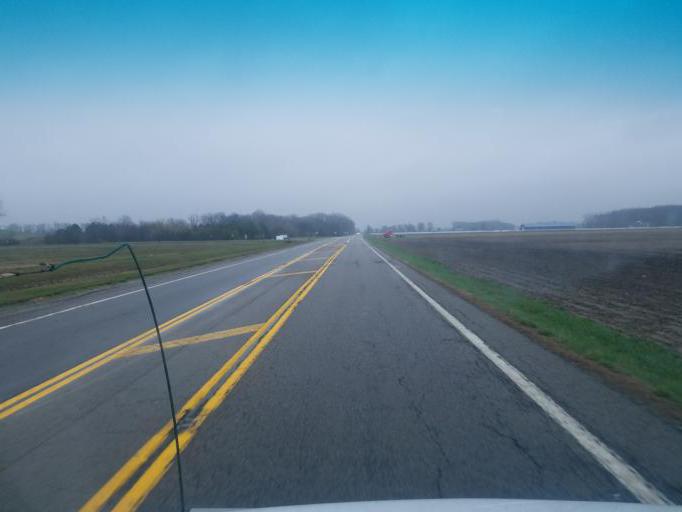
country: US
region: Ohio
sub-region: Wood County
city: Weston
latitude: 41.3722
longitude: -83.7398
